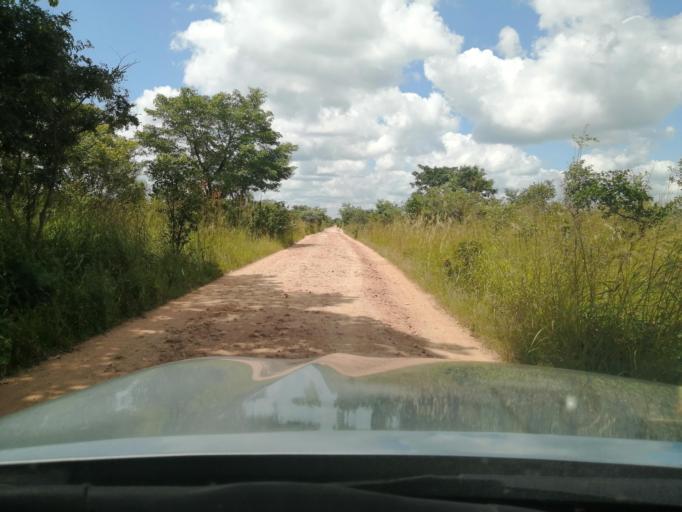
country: ZM
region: Lusaka
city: Lusaka
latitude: -15.1489
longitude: 27.9370
